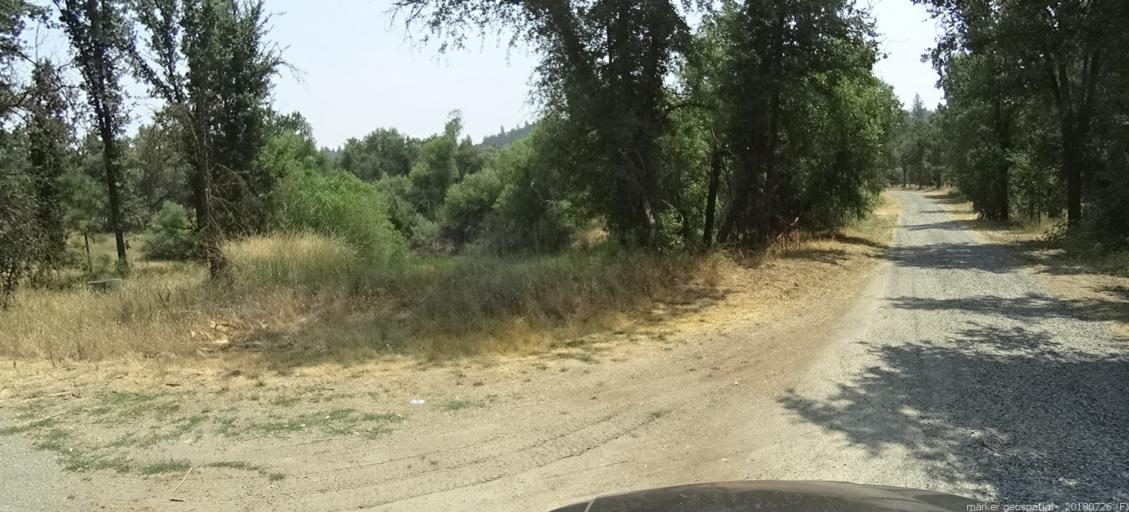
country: US
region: California
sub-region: Madera County
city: Oakhurst
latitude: 37.2878
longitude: -119.6505
